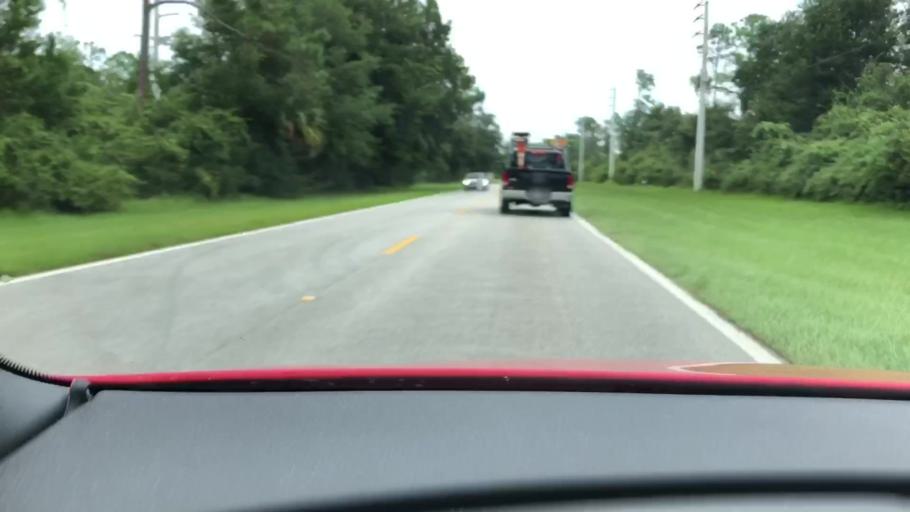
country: US
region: Florida
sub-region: Flagler County
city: Palm Coast
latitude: 29.5453
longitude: -81.2123
